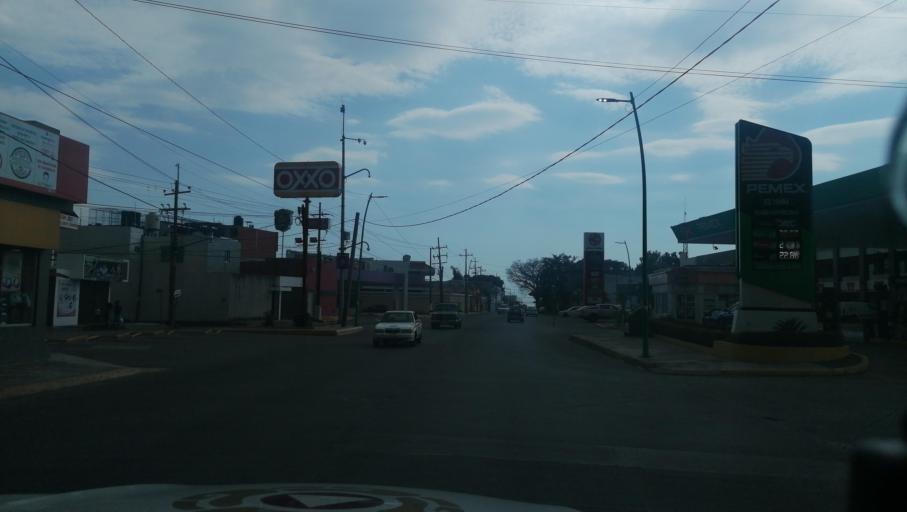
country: MX
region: Chiapas
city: Tapachula
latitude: 14.9215
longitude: -92.2551
